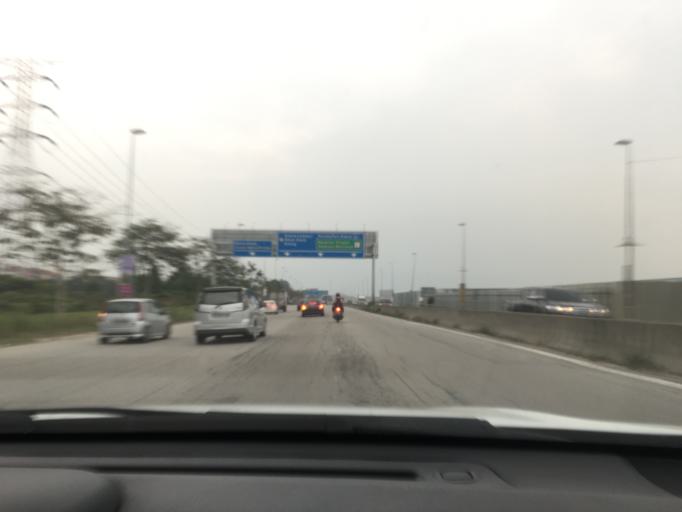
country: MY
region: Selangor
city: Klang
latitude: 3.0987
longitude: 101.4429
